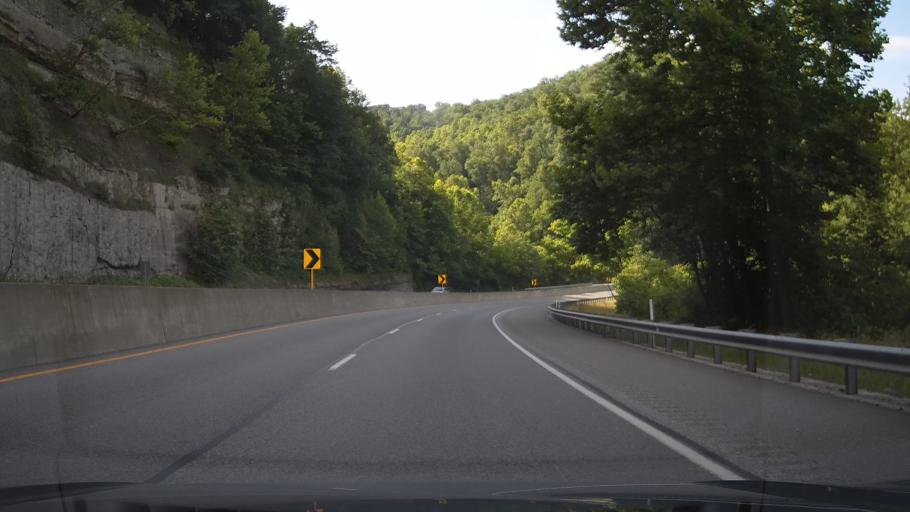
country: US
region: Kentucky
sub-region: Lawrence County
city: Louisa
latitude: 37.9771
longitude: -82.6716
